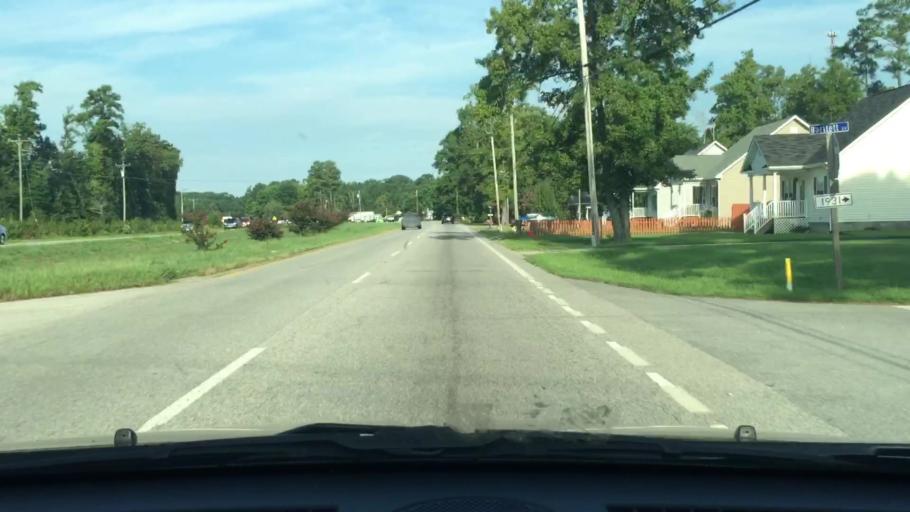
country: US
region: Virginia
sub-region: Isle of Wight County
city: Carrollton
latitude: 36.9428
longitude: -76.5493
